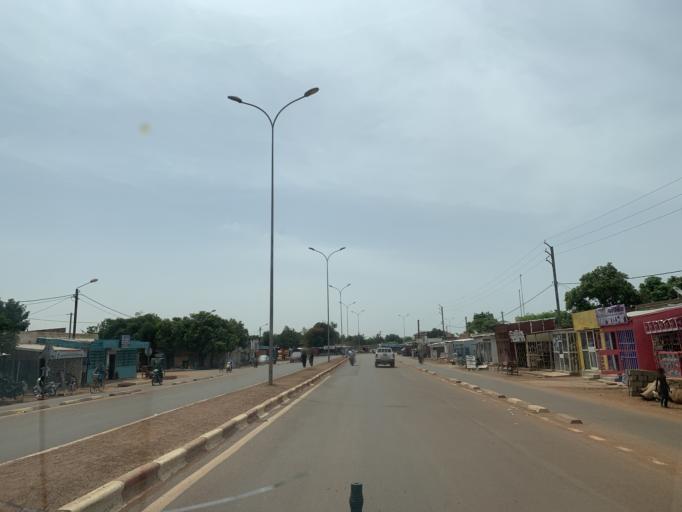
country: BF
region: Centre
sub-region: Kadiogo Province
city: Ouagadougou
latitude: 12.3394
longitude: -1.5130
